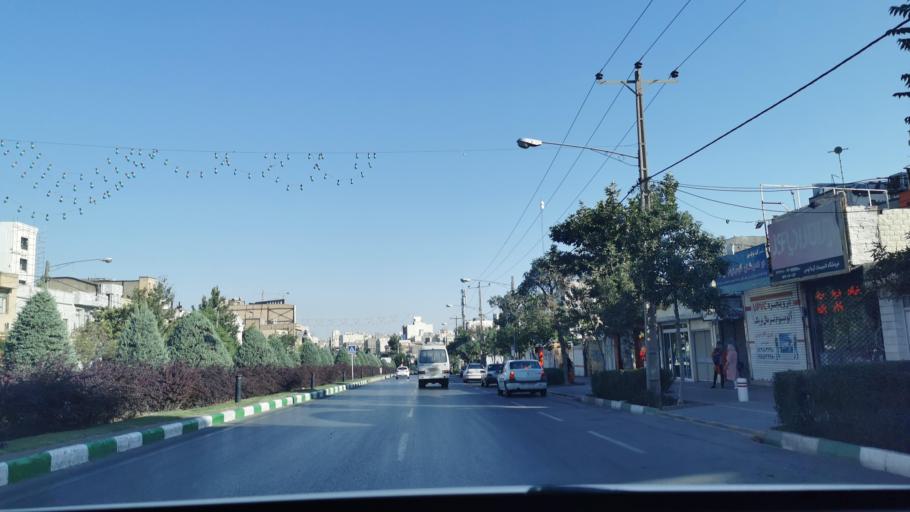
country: IR
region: Razavi Khorasan
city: Mashhad
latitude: 36.3094
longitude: 59.5062
